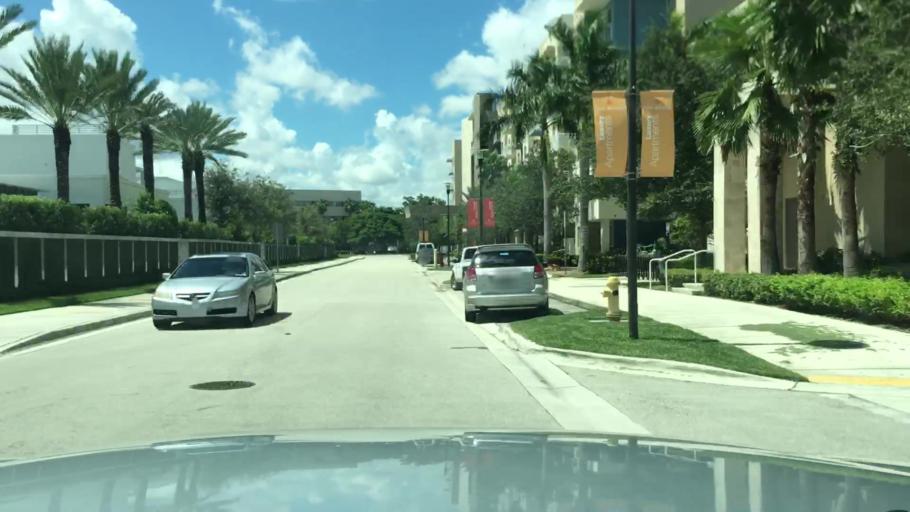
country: US
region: Florida
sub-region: Miami-Dade County
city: Doral
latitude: 25.8067
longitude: -80.3333
